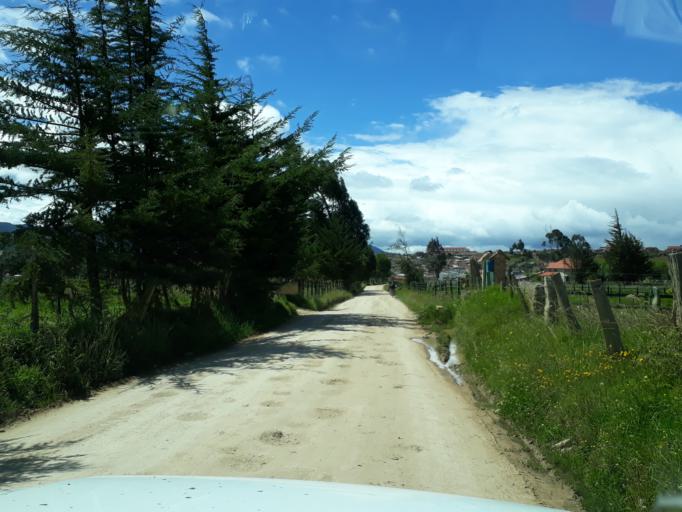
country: CO
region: Cundinamarca
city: Guasca
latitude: 4.8572
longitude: -73.8791
